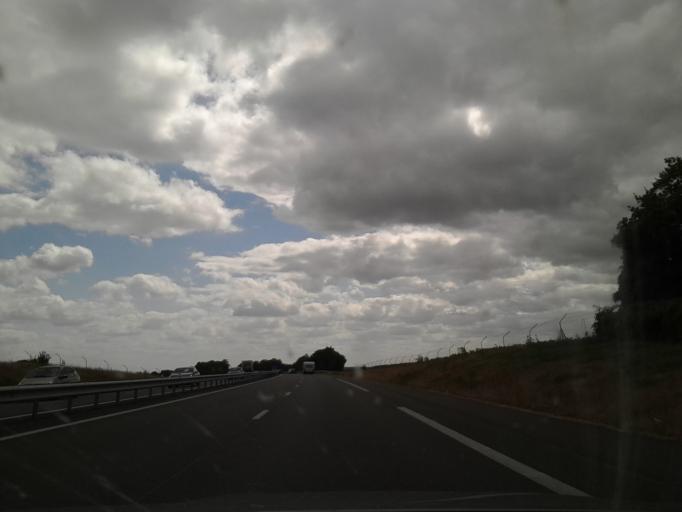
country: FR
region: Centre
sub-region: Departement du Cher
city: Levet
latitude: 46.8456
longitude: 2.4193
